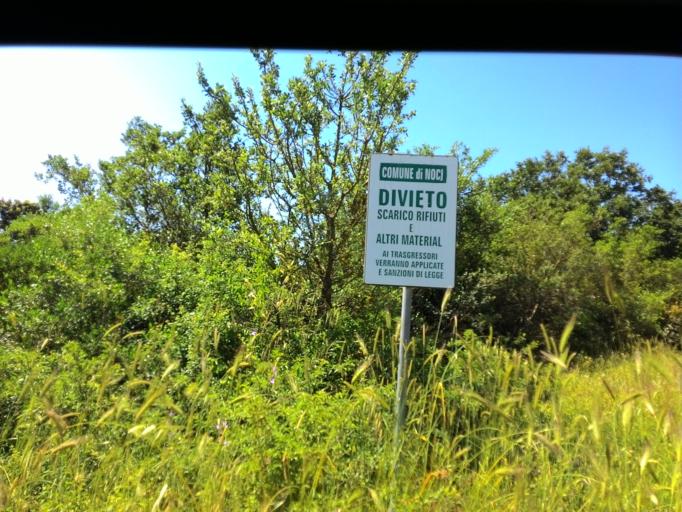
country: IT
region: Apulia
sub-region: Provincia di Bari
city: Noci
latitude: 40.8184
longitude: 17.1313
